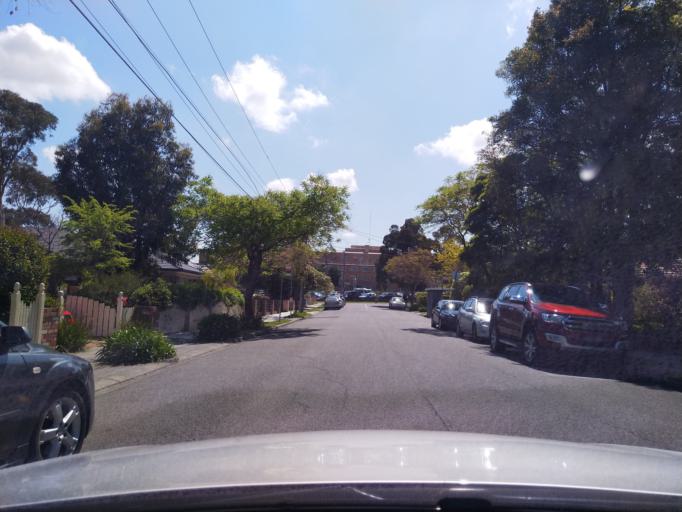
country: AU
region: Victoria
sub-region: Banyule
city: Bellfield
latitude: -37.7582
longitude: 145.0470
